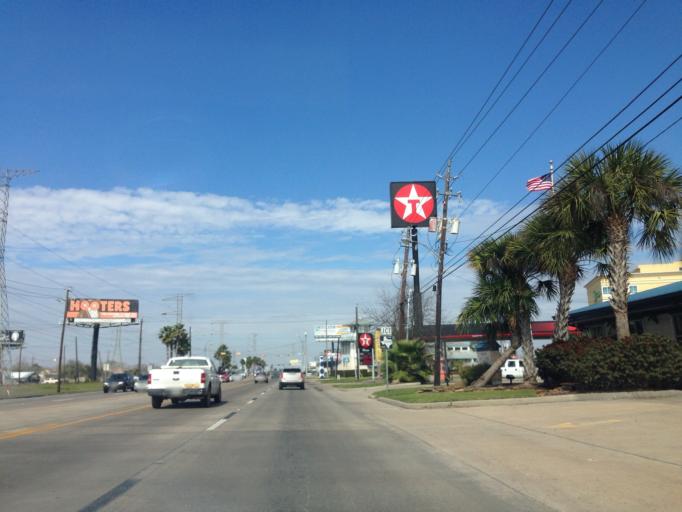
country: US
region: Texas
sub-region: Galveston County
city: Kemah
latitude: 29.5396
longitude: -95.0190
